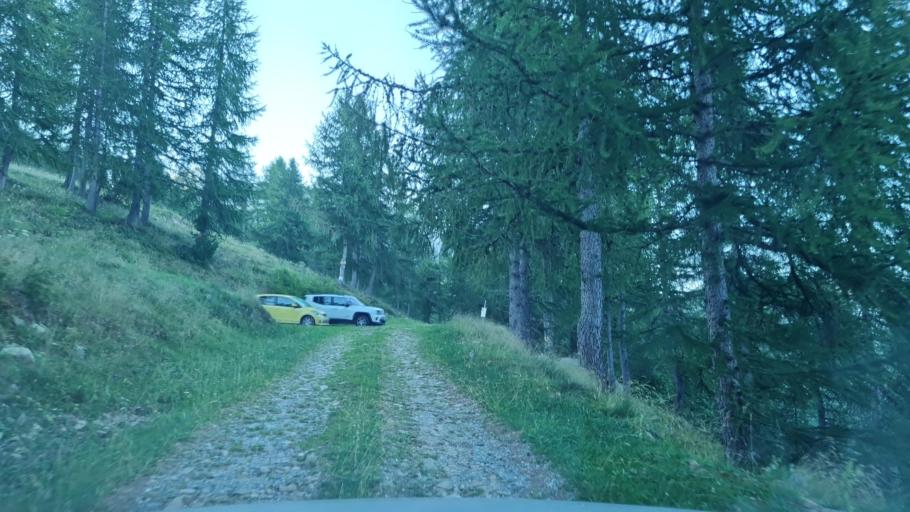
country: IT
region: Aosta Valley
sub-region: Valle d'Aosta
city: Fontainemore
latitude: 45.6196
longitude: 7.8782
